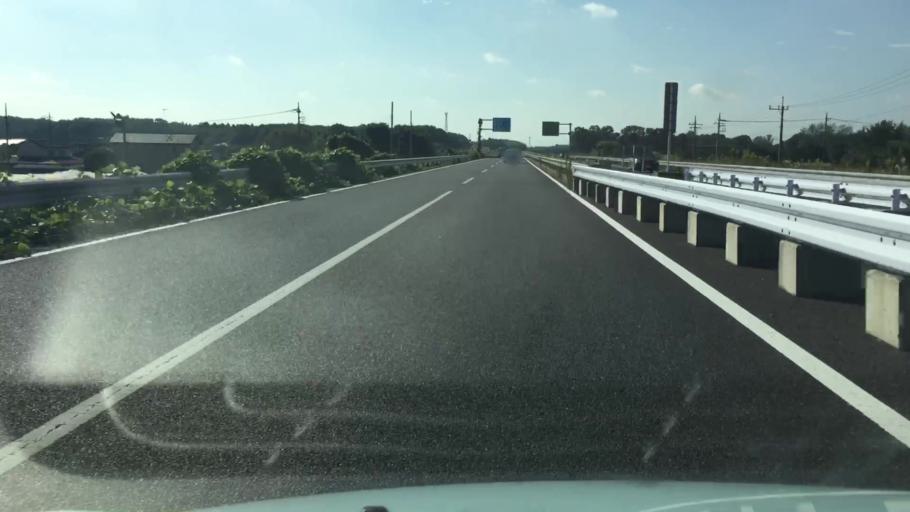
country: JP
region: Tochigi
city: Mooka
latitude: 36.5064
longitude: 139.9878
